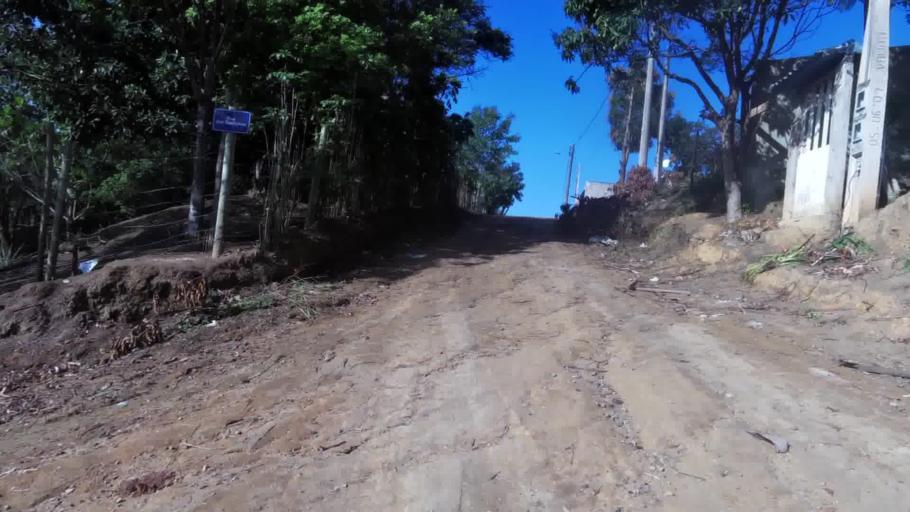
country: BR
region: Espirito Santo
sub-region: Piuma
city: Piuma
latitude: -20.8151
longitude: -40.6232
